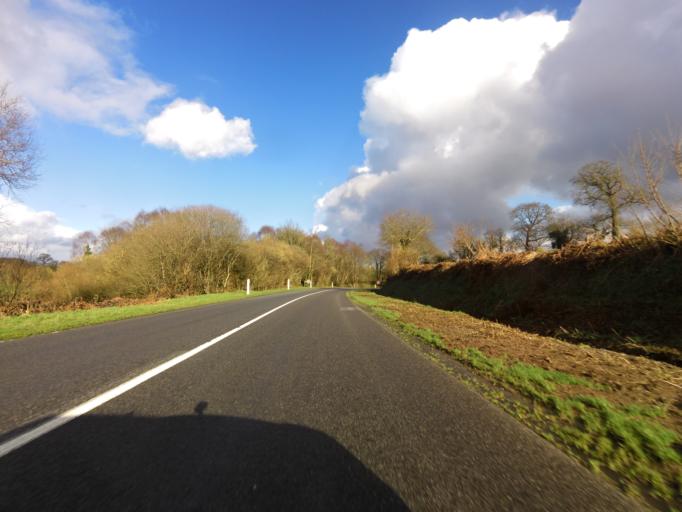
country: FR
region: Brittany
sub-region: Departement du Morbihan
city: Langonnet
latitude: 48.1425
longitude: -3.5347
